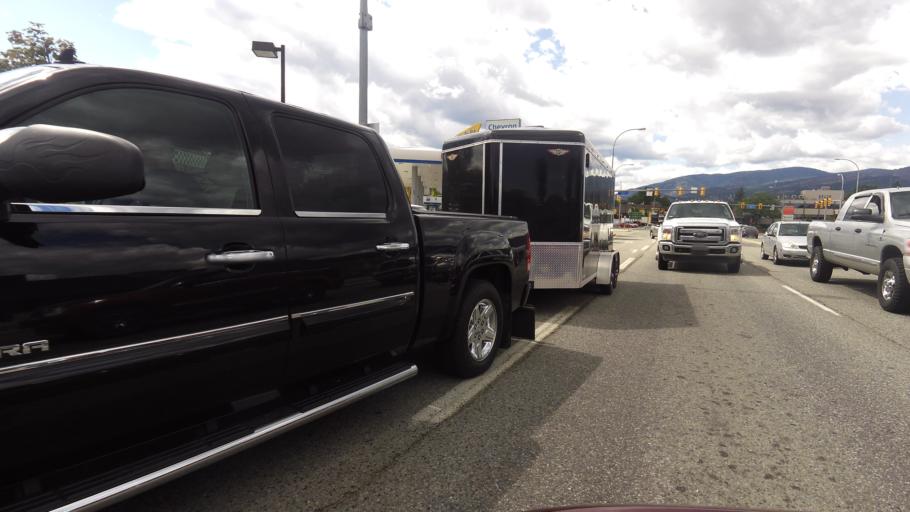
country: CA
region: British Columbia
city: Kelowna
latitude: 49.8835
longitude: -119.4948
